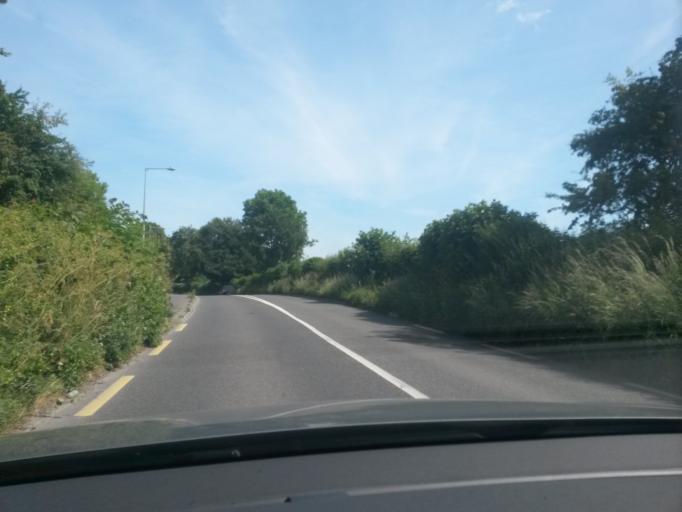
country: IE
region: Leinster
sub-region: Wicklow
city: Blessington
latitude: 53.1737
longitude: -6.5539
